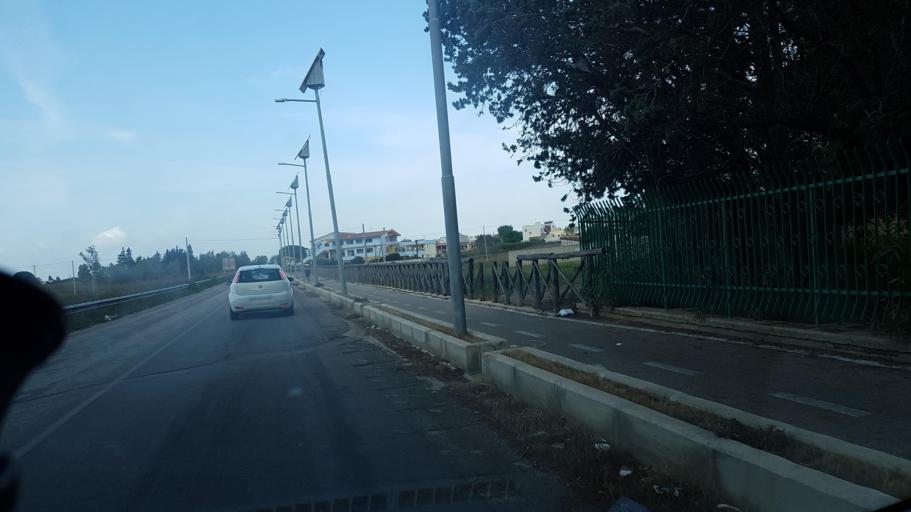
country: IT
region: Apulia
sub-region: Provincia di Brindisi
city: San Pietro Vernotico
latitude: 40.4802
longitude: 17.9970
